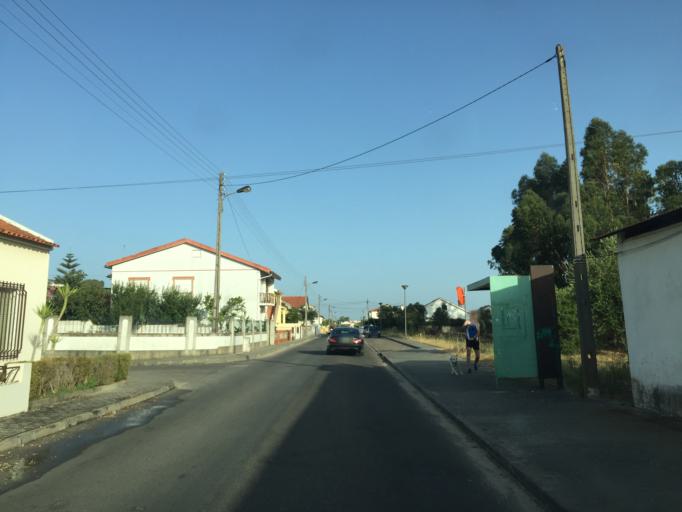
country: PT
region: Santarem
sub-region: Entroncamento
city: Entroncamento
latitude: 39.4724
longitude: -8.4456
